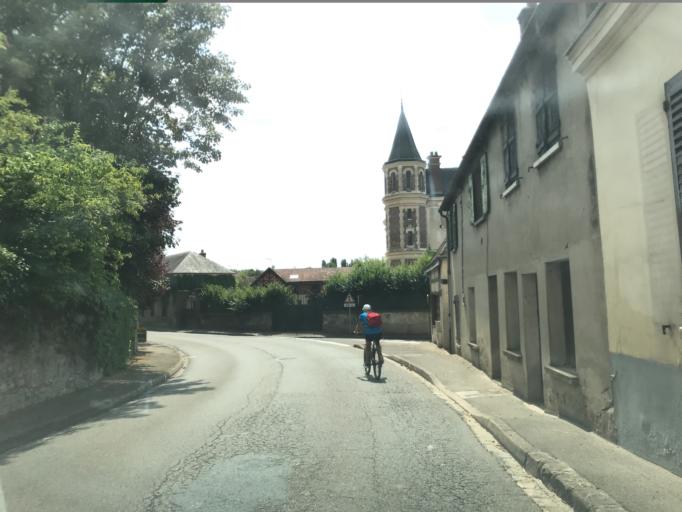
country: FR
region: Centre
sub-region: Departement d'Eure-et-Loir
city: Anet
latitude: 48.8570
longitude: 1.4361
